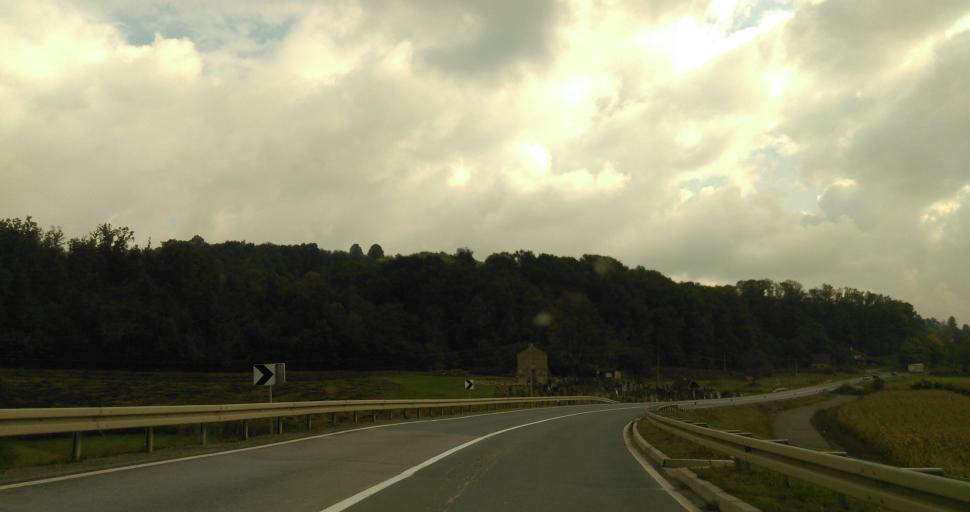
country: RS
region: Central Serbia
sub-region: Kolubarski Okrug
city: Ljig
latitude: 44.1990
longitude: 20.2777
